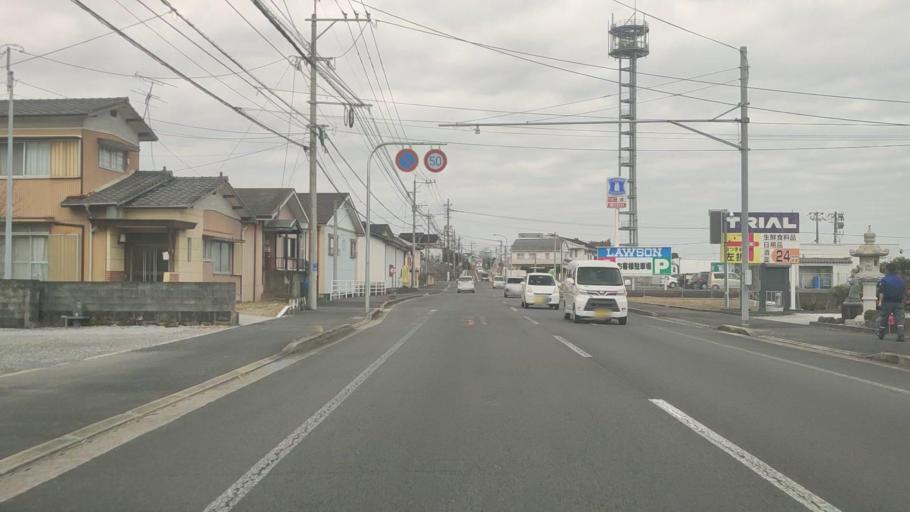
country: JP
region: Nagasaki
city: Shimabara
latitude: 32.8141
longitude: 130.3573
